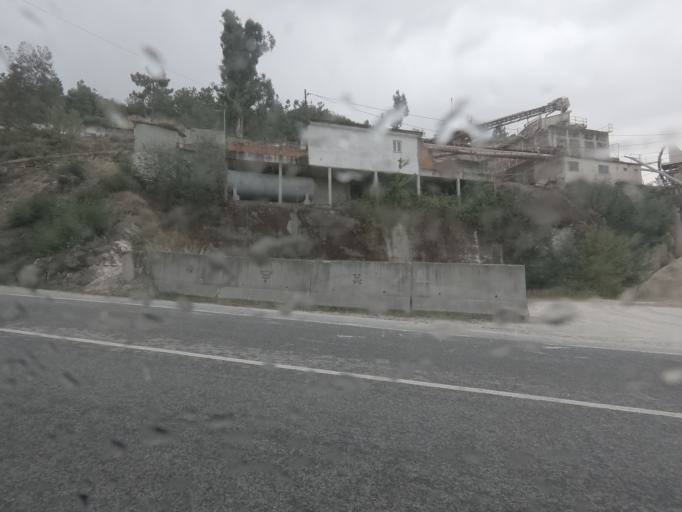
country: PT
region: Viseu
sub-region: Armamar
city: Armamar
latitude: 41.1269
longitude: -7.7341
